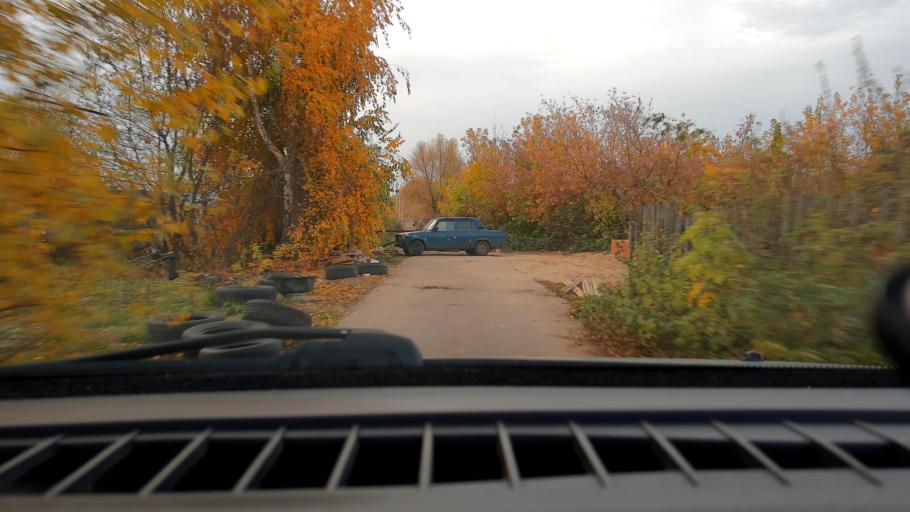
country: RU
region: Nizjnij Novgorod
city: Afonino
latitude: 56.2916
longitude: 44.1034
